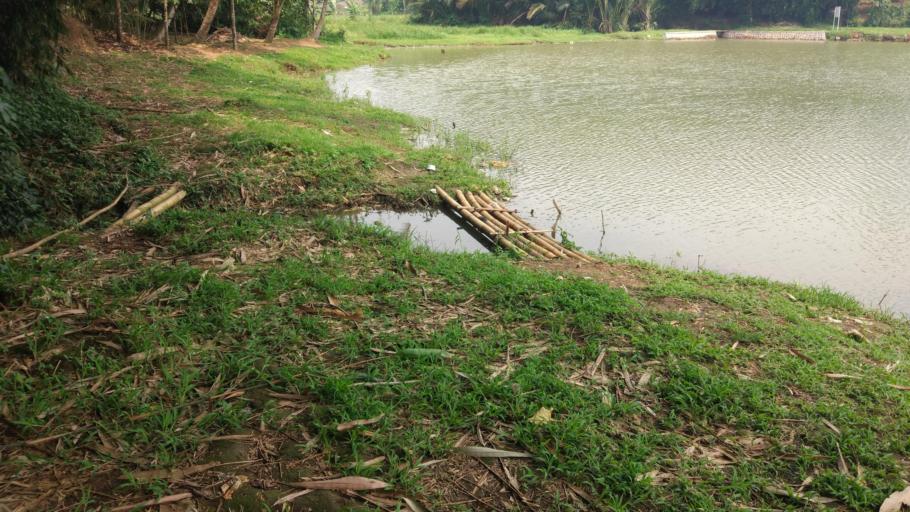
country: ID
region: West Java
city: Ciampea
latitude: -6.5748
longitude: 106.7306
